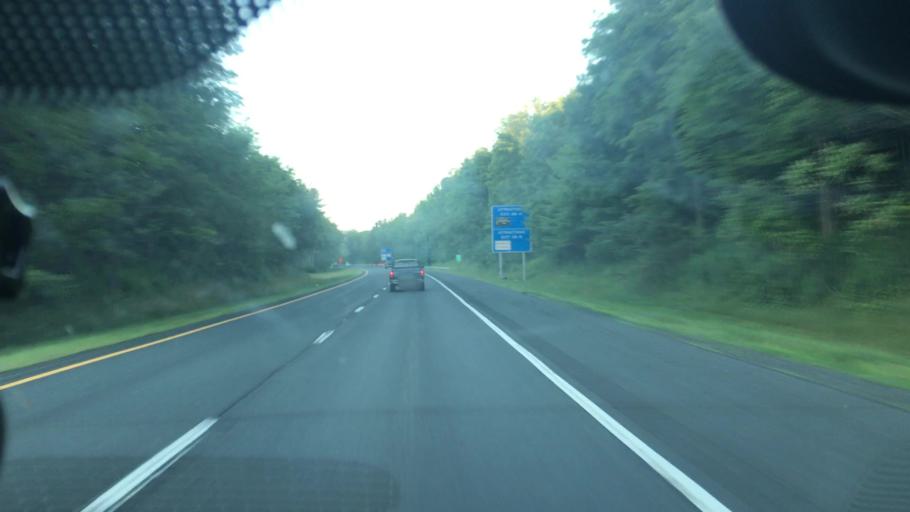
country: US
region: Massachusetts
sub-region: Franklin County
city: Bernardston
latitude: 42.6570
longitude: -72.5502
